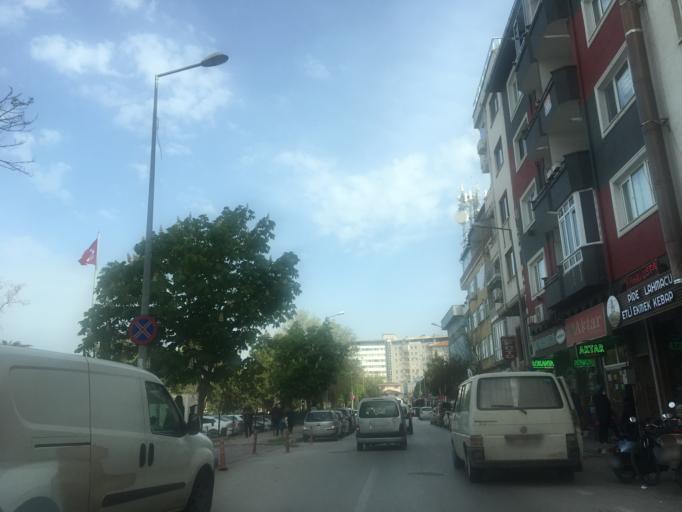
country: TR
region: Bursa
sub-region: Mudanya
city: Mudanya
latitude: 40.3741
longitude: 28.8871
